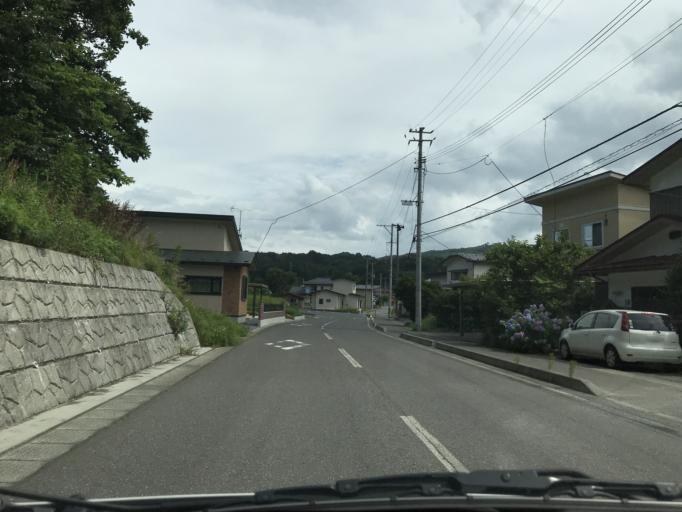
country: JP
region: Iwate
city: Tono
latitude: 39.3240
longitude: 141.5381
